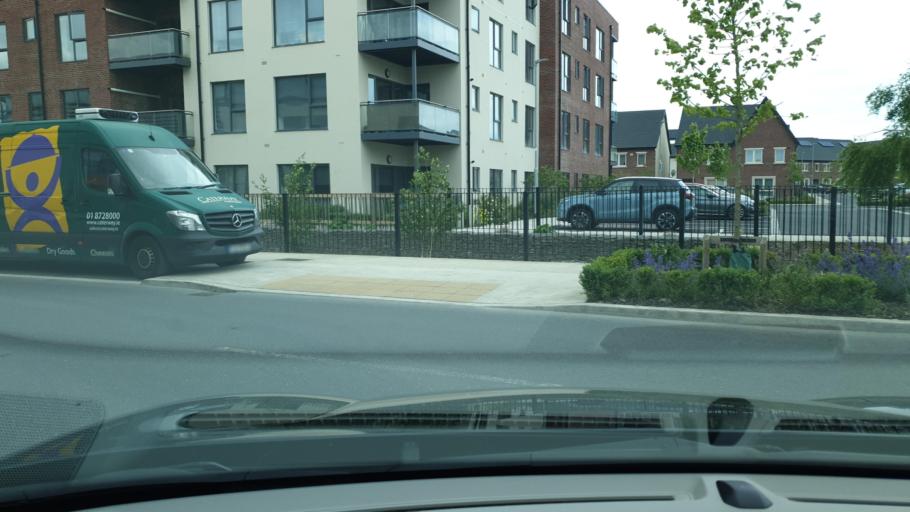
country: IE
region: Leinster
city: Lucan
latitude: 53.3455
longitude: -6.4738
